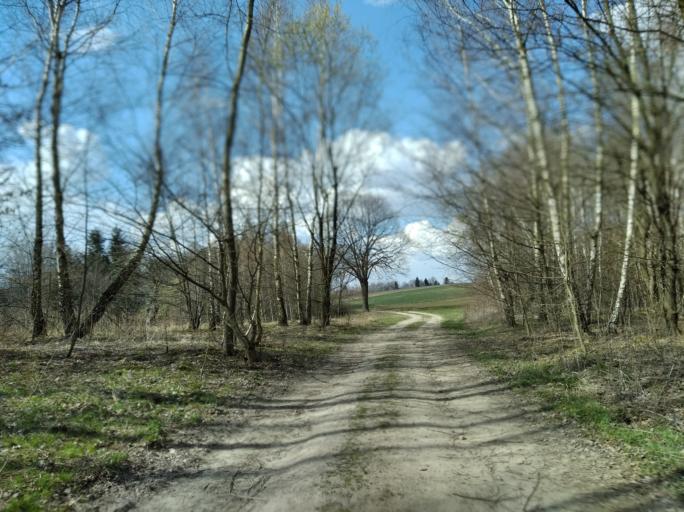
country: PL
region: Subcarpathian Voivodeship
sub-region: Powiat strzyzowski
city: Strzyzow
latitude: 49.9262
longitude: 21.7296
